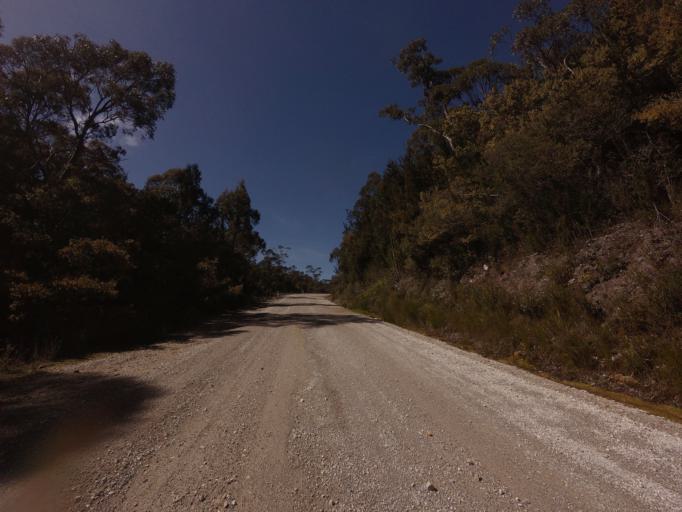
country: AU
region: Tasmania
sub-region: Huon Valley
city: Geeveston
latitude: -42.8173
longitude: 146.3869
